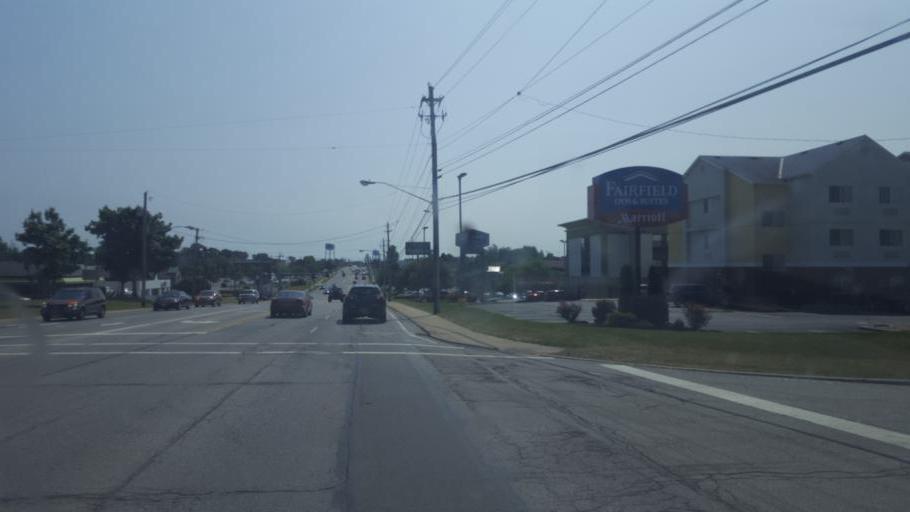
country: US
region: Ohio
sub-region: Richland County
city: Ontario
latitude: 40.7819
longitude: -82.5903
